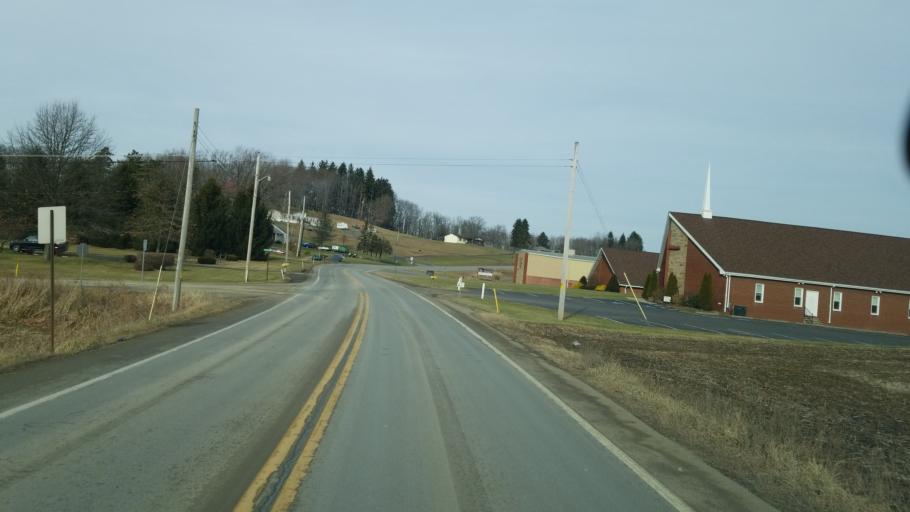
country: US
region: Pennsylvania
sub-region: Jefferson County
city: Punxsutawney
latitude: 40.9227
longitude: -78.9894
